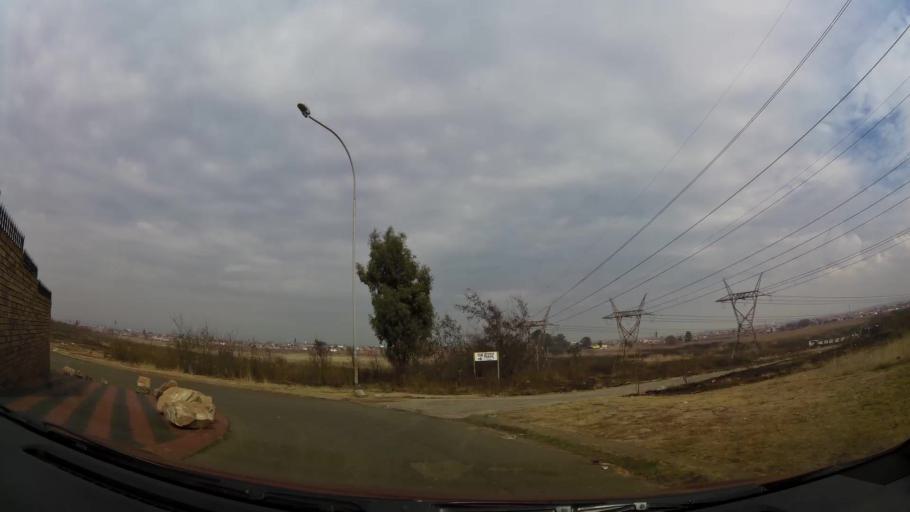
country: ZA
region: Gauteng
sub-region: City of Johannesburg Metropolitan Municipality
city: Soweto
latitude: -26.2673
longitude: 27.8248
